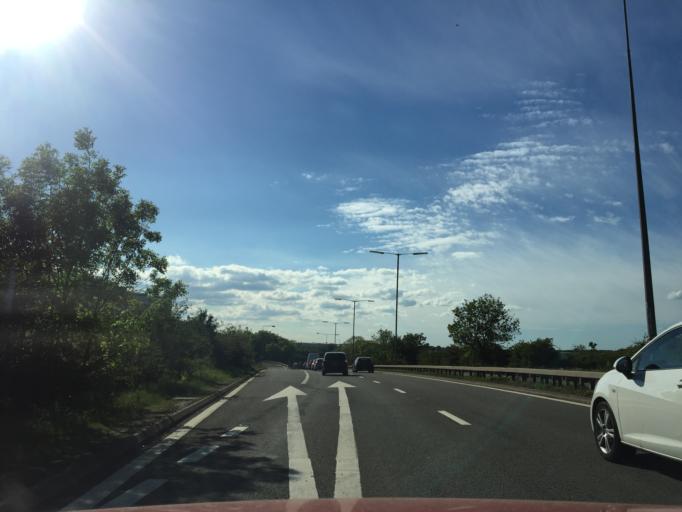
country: GB
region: England
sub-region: Warwickshire
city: Ryton on Dunsmore
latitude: 52.3722
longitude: -1.4513
